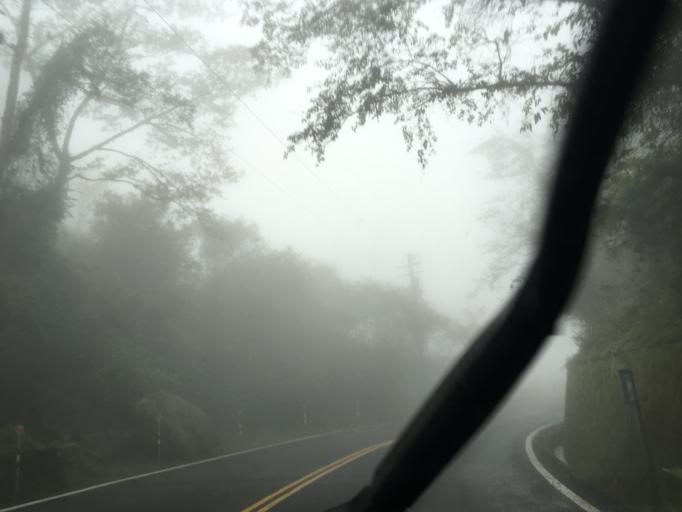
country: TW
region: Taiwan
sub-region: Hualien
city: Hualian
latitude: 24.1987
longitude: 121.4330
